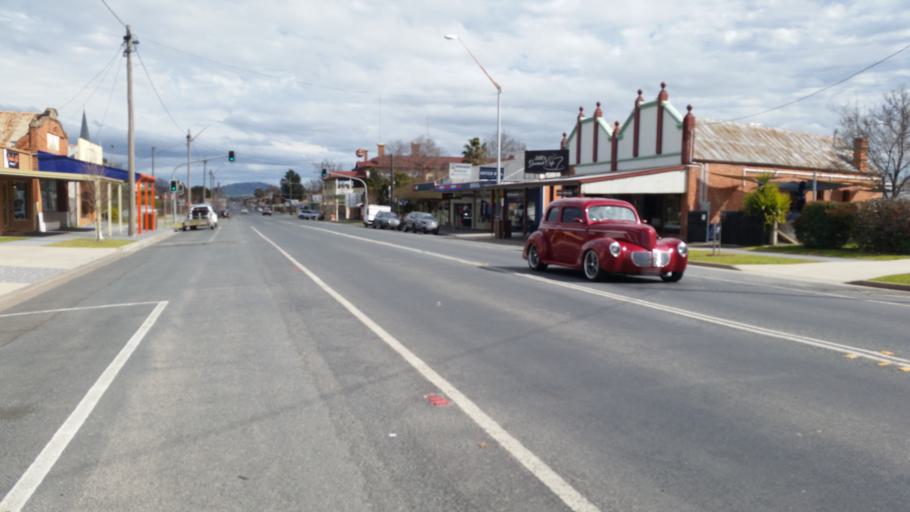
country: AU
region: New South Wales
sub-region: Greater Hume Shire
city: Holbrook
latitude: -35.7215
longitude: 147.3156
